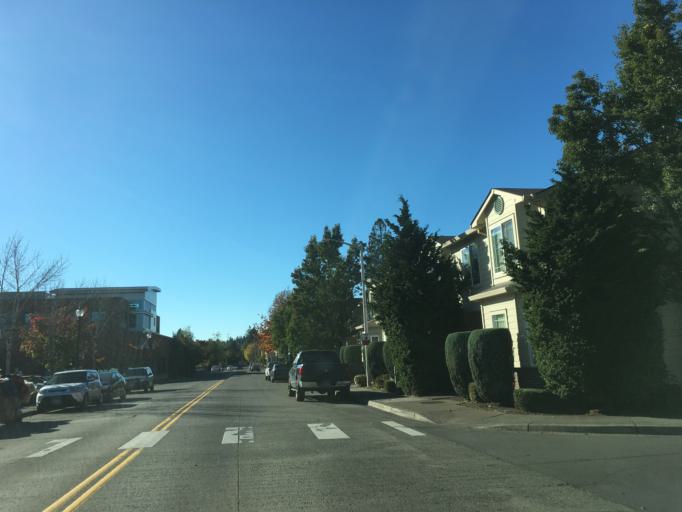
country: US
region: Oregon
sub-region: Multnomah County
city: Gresham
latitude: 45.5030
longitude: -122.4235
